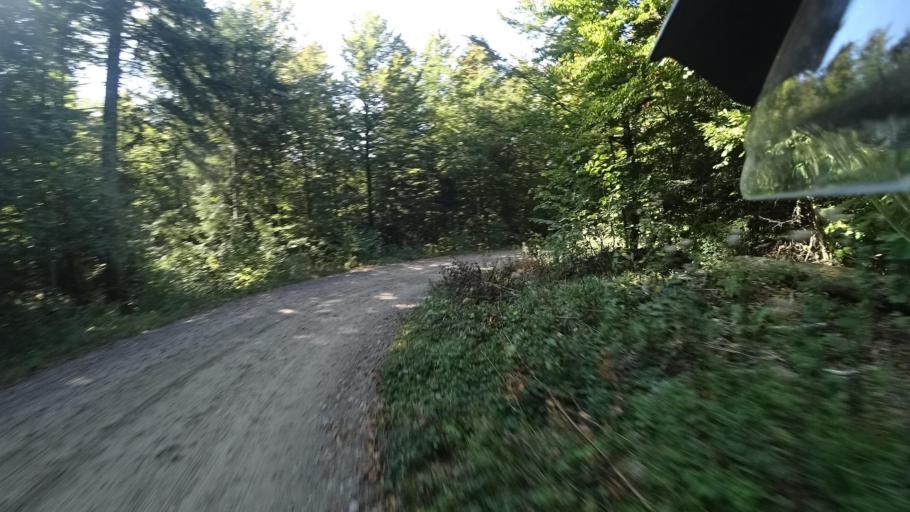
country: HR
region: Karlovacka
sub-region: Grad Ogulin
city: Ogulin
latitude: 45.2316
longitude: 15.1314
